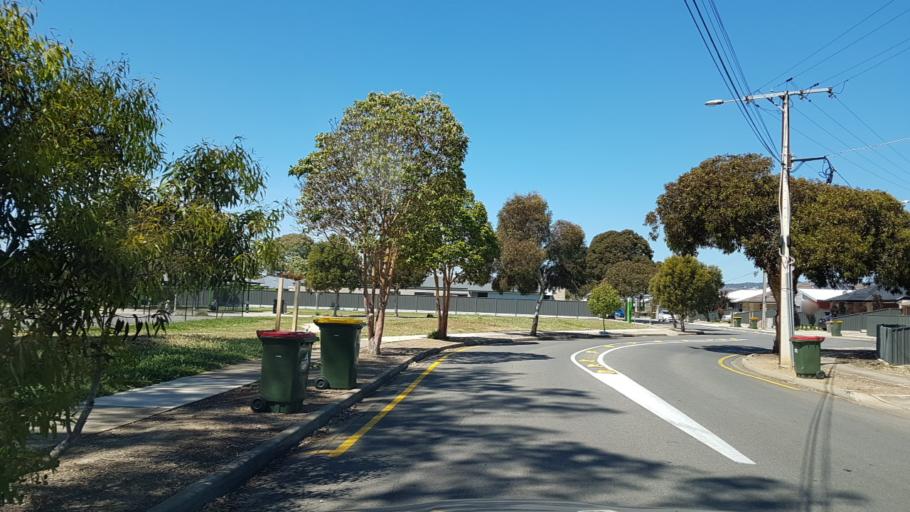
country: AU
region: South Australia
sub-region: Marion
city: Plympton Park
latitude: -34.9785
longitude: 138.5499
